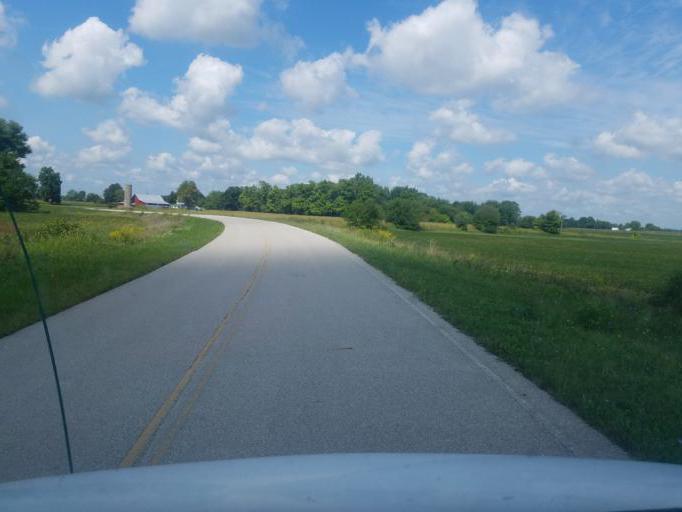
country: US
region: Ohio
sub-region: Marion County
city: Prospect
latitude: 40.4255
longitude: -83.1586
